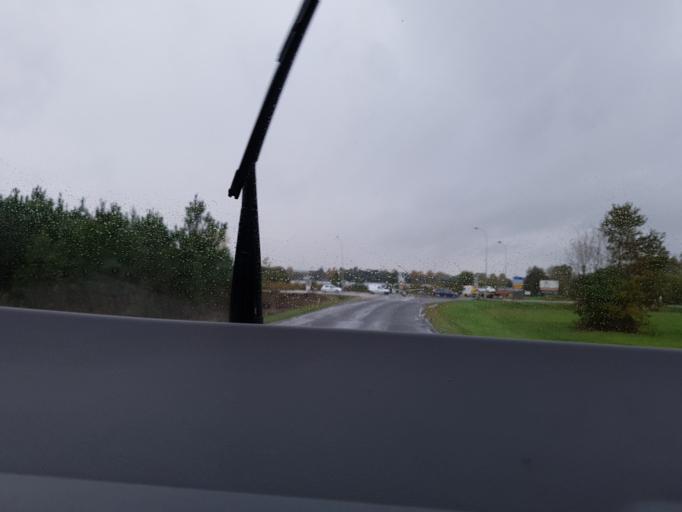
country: FR
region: Aquitaine
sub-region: Departement de la Gironde
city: Etauliers
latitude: 45.2465
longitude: -0.5564
